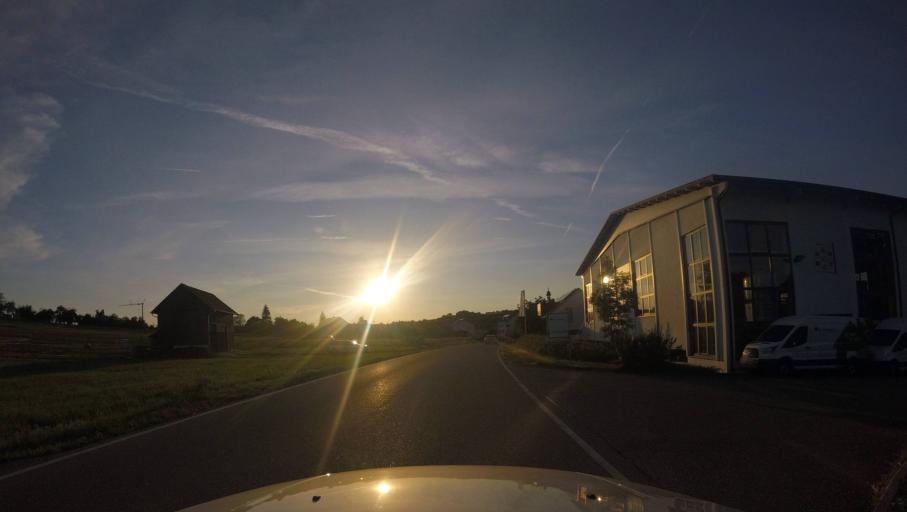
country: DE
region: Baden-Wuerttemberg
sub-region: Regierungsbezirk Stuttgart
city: Rudersberg
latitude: 48.9205
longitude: 9.5075
